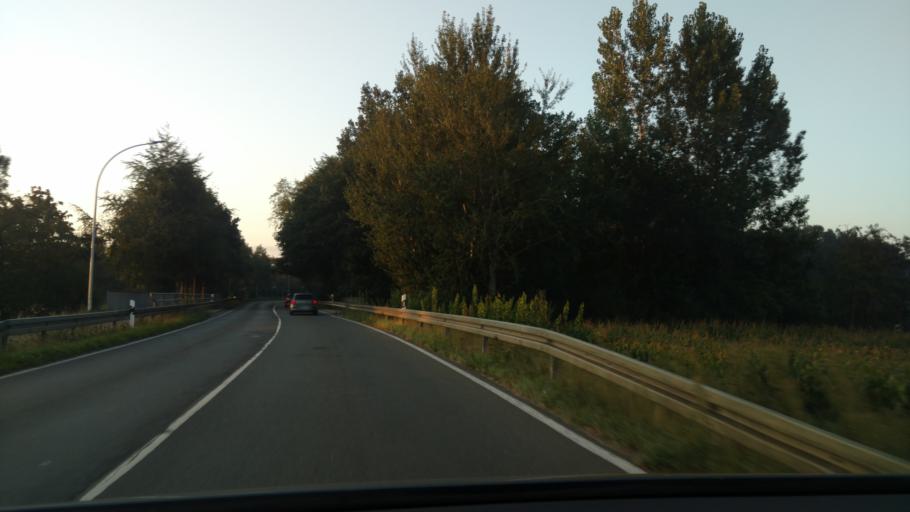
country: DE
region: North Rhine-Westphalia
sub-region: Regierungsbezirk Munster
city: Borken
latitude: 51.8563
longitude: 6.8417
